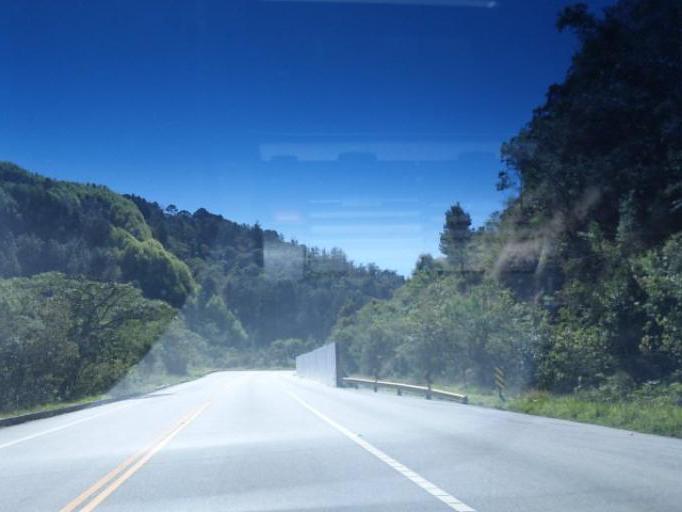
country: BR
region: Sao Paulo
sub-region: Campos Do Jordao
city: Campos do Jordao
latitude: -22.7802
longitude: -45.6111
